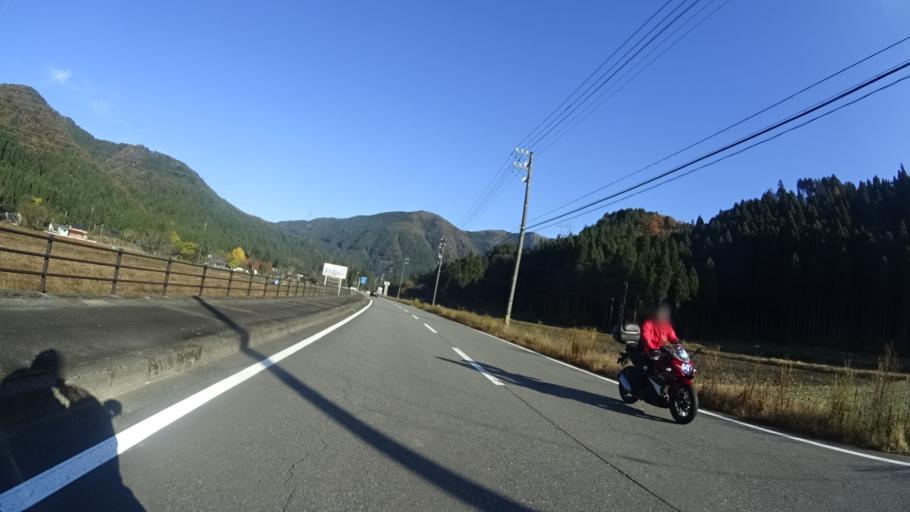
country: JP
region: Fukui
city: Maruoka
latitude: 36.1633
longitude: 136.3326
